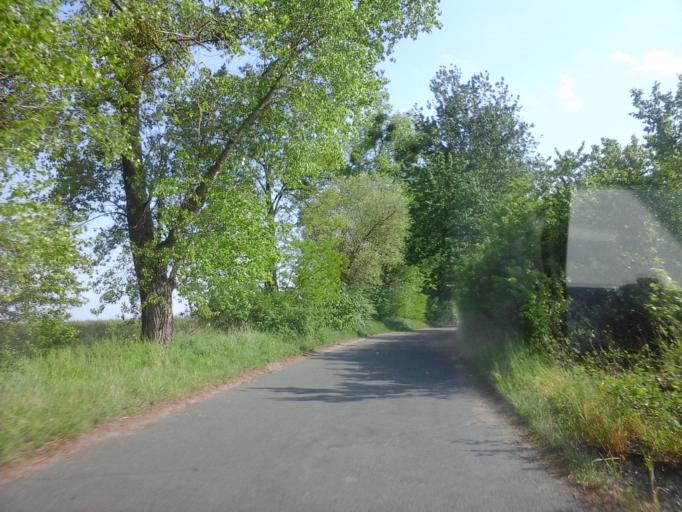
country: PL
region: West Pomeranian Voivodeship
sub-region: Powiat choszczenski
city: Choszczno
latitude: 53.1196
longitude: 15.3983
